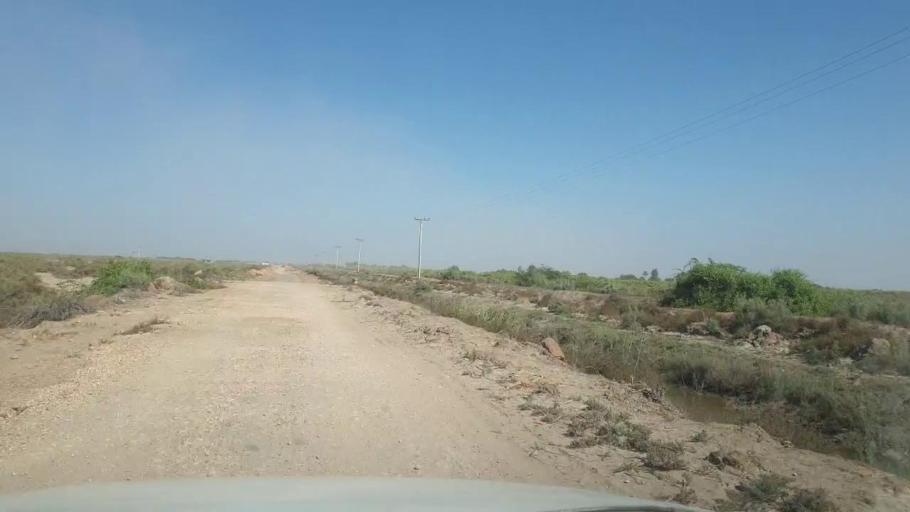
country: PK
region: Sindh
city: Mirpur Sakro
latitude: 24.4605
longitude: 67.7094
